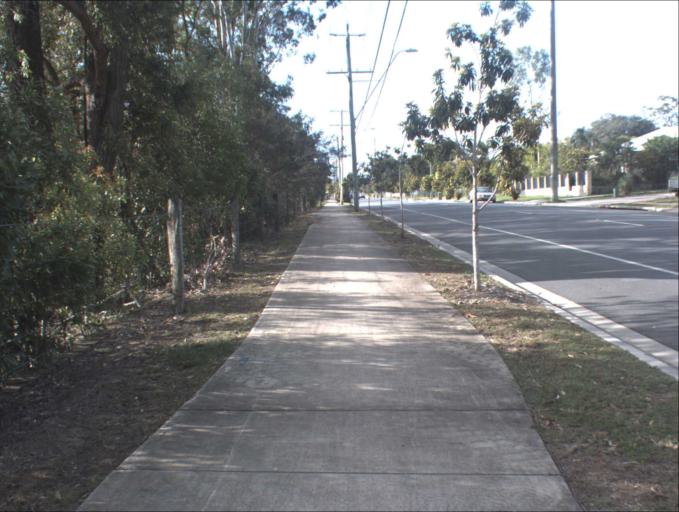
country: AU
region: Queensland
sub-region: Logan
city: Waterford West
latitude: -27.6907
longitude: 153.1196
